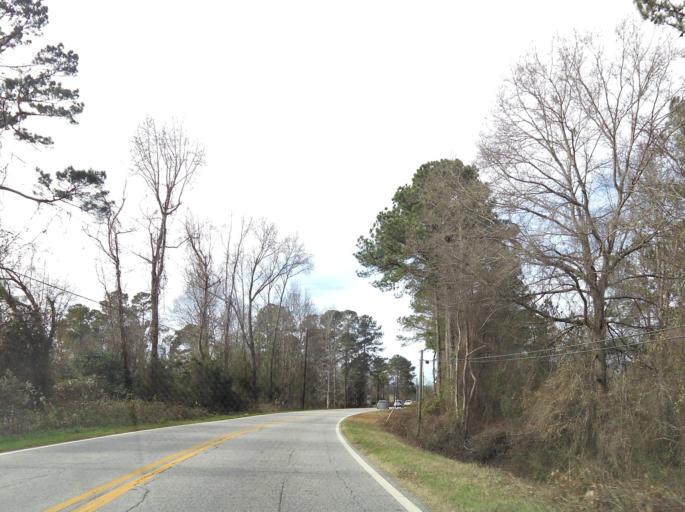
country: US
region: Georgia
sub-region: Bibb County
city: West Point
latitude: 32.8043
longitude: -83.7699
